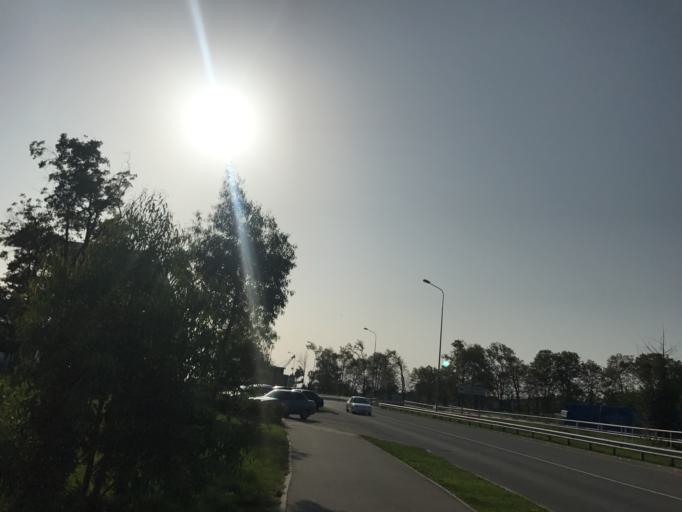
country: RU
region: Krasnodarskiy
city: Adler
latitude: 43.4144
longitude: 39.9357
